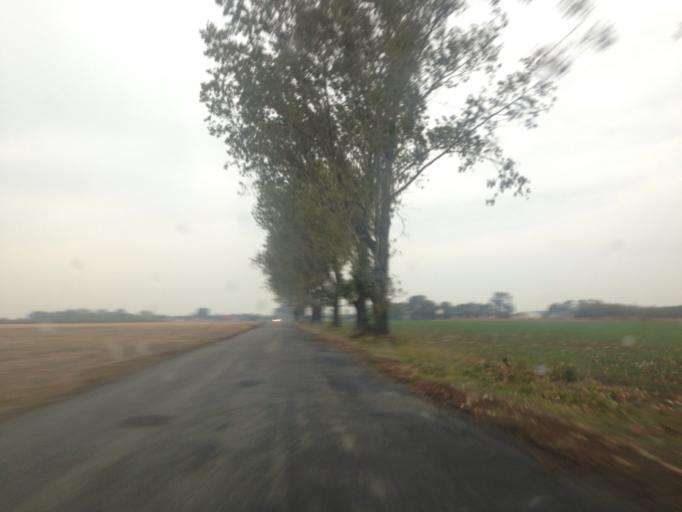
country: PL
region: Greater Poland Voivodeship
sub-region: Powiat poznanski
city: Kleszczewo
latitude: 52.3543
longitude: 17.1423
